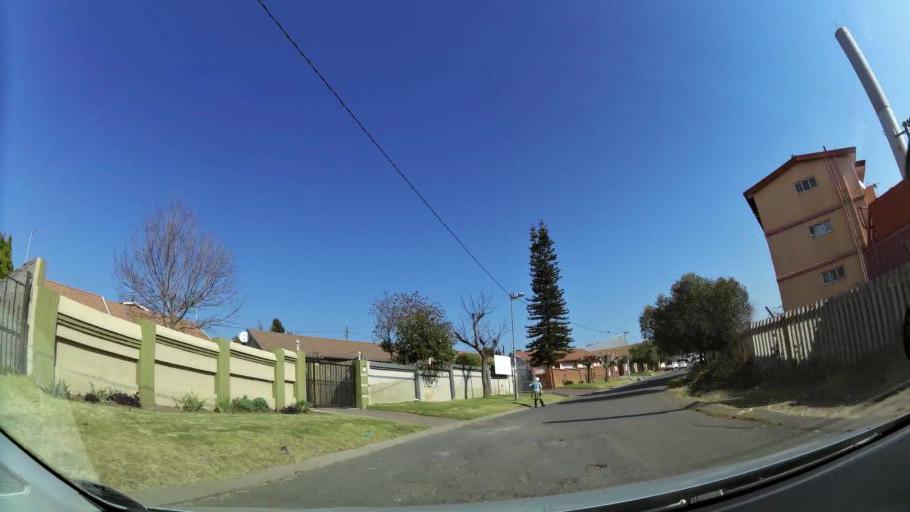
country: ZA
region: Gauteng
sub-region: City of Johannesburg Metropolitan Municipality
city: Modderfontein
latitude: -26.1083
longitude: 28.0933
